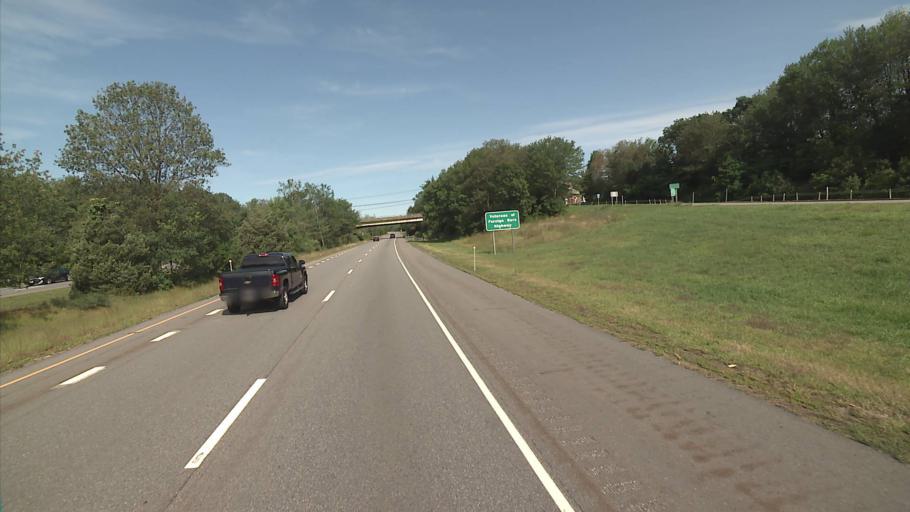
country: US
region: Connecticut
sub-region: New London County
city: Colchester
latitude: 41.5694
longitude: -72.3365
